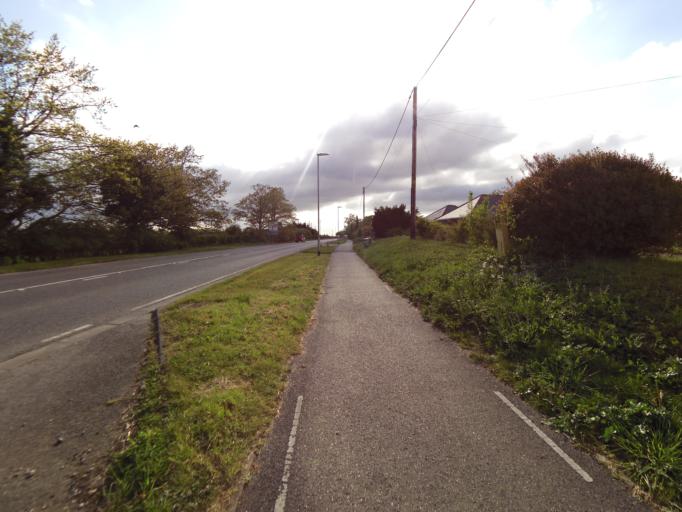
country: GB
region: England
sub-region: Cambridgeshire
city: Fulbourn
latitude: 52.2166
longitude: 0.2207
